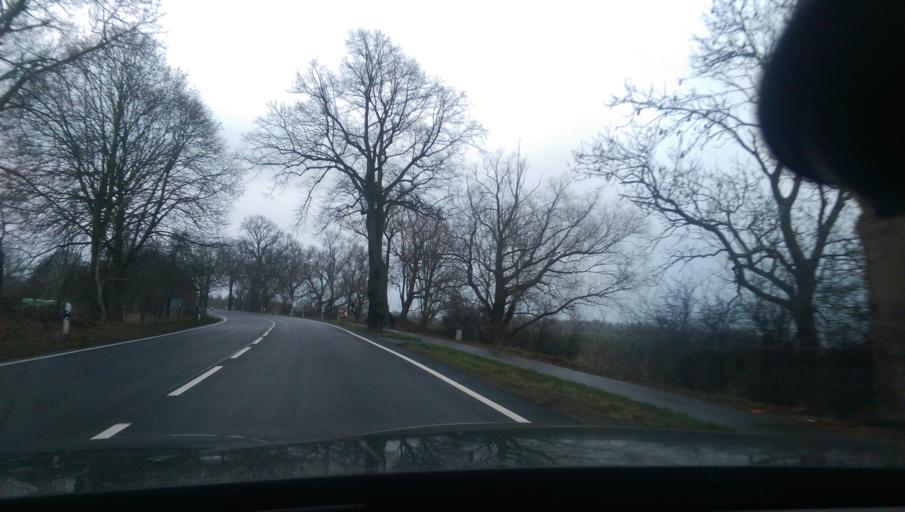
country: DE
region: Lower Saxony
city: Verden
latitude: 52.8921
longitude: 9.2200
